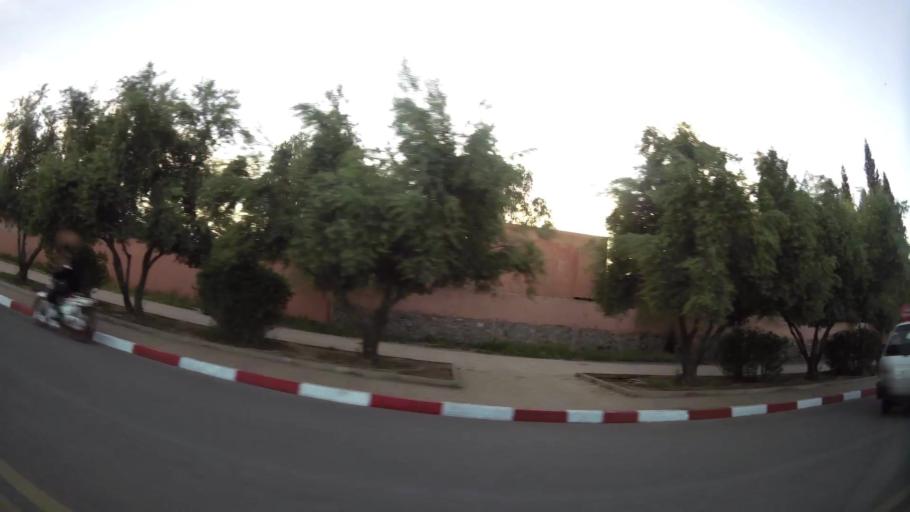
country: MA
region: Marrakech-Tensift-Al Haouz
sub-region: Marrakech
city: Marrakesh
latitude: 31.6395
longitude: -8.0313
